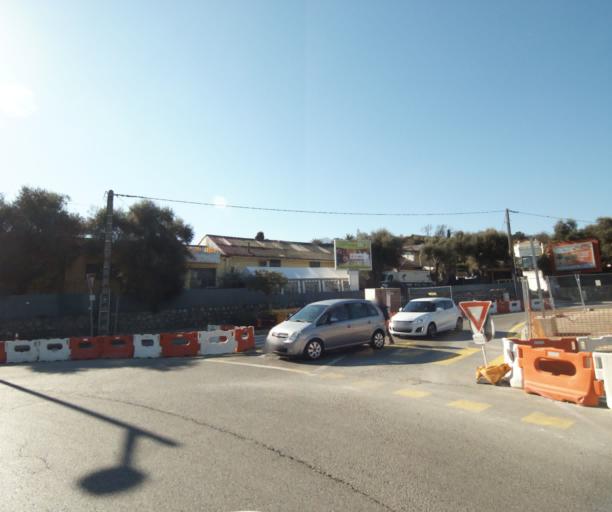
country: FR
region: Provence-Alpes-Cote d'Azur
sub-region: Departement des Alpes-Maritimes
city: Antibes
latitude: 43.5925
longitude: 7.1154
